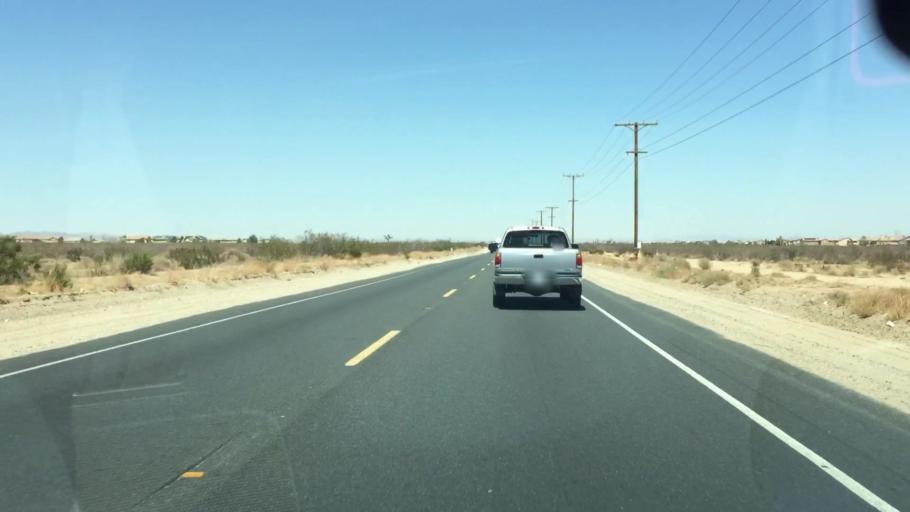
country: US
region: California
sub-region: San Bernardino County
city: Mountain View Acres
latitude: 34.4742
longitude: -117.3995
